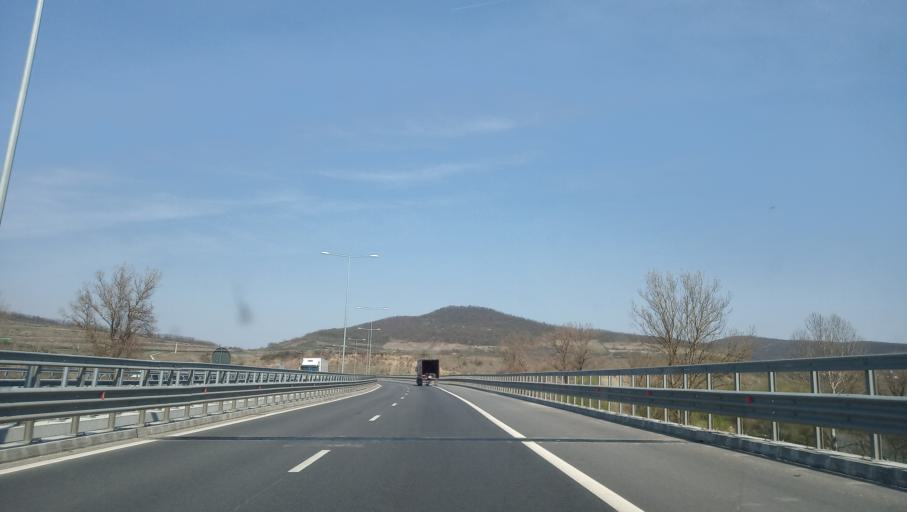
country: RO
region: Alba
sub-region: Municipiul Aiud
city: Aiud
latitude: 46.3361
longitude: 23.7322
